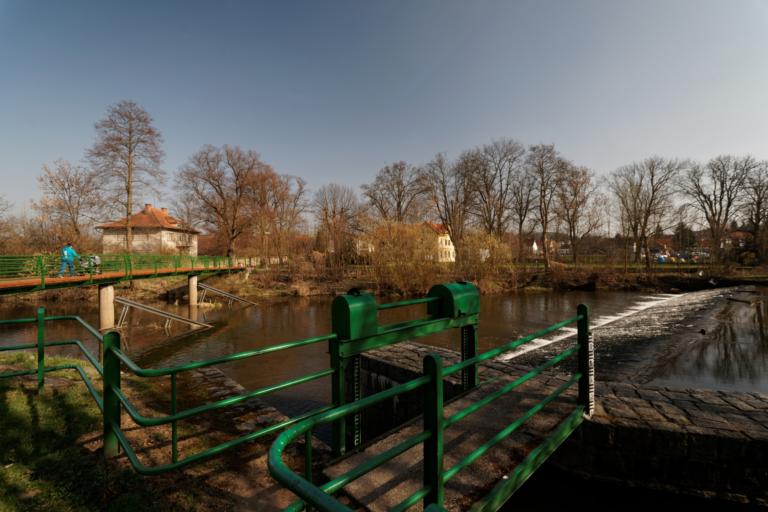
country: CZ
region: Plzensky
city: Horsovsky Tyn
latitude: 49.5287
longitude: 12.9452
